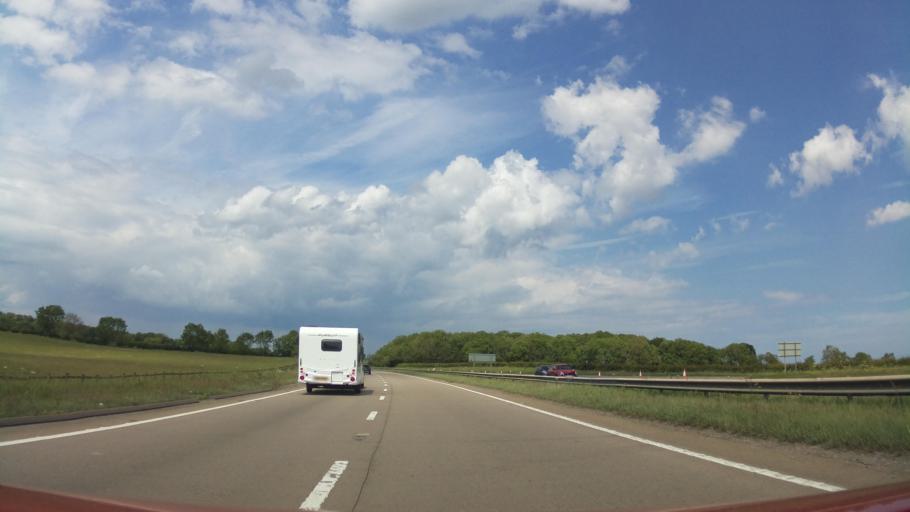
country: GB
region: England
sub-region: Hartlepool
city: Elwick
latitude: 54.6391
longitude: -1.2995
